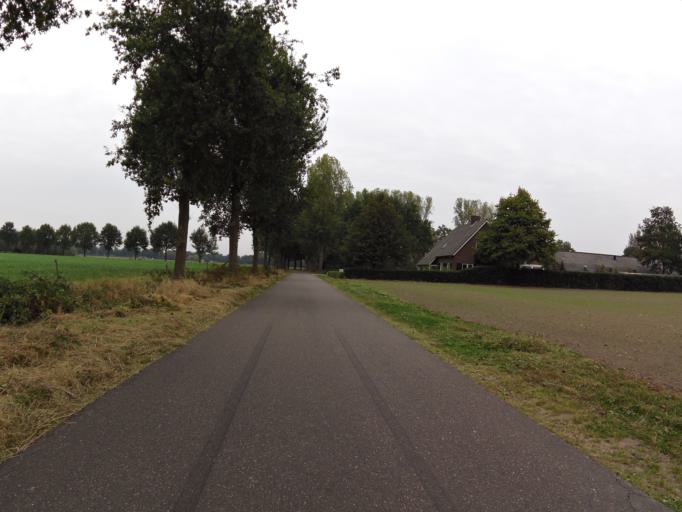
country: NL
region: North Brabant
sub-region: Gemeente Haaren
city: Haaren
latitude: 51.6143
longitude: 5.2259
